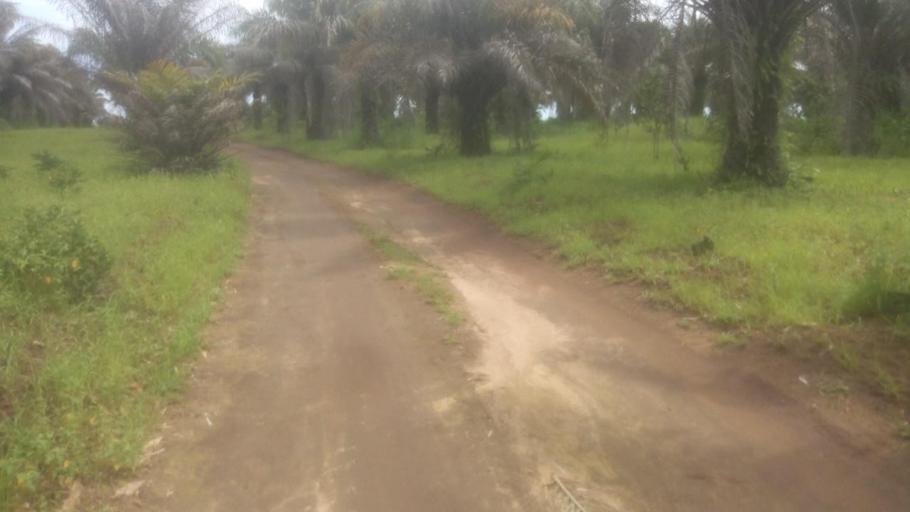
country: SL
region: Northern Province
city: Masoyila
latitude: 8.5918
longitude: -13.1911
